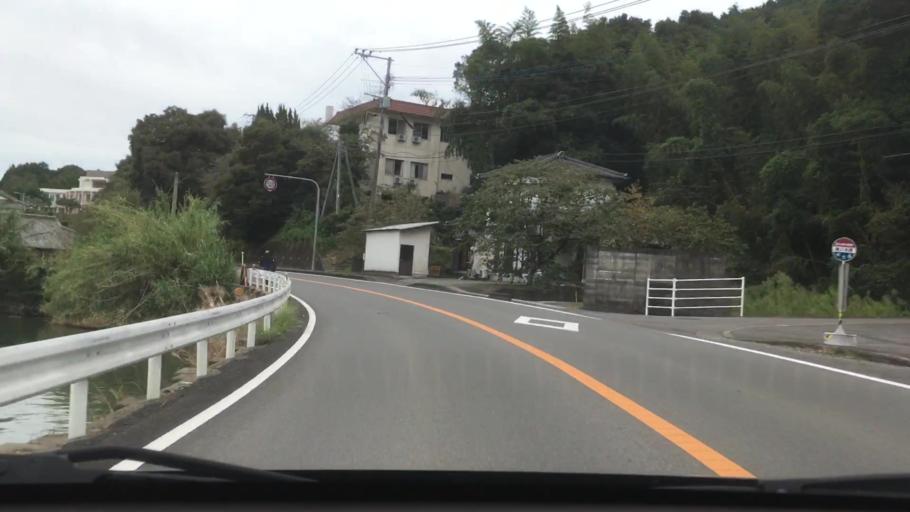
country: JP
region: Nagasaki
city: Sasebo
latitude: 33.0167
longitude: 129.7329
